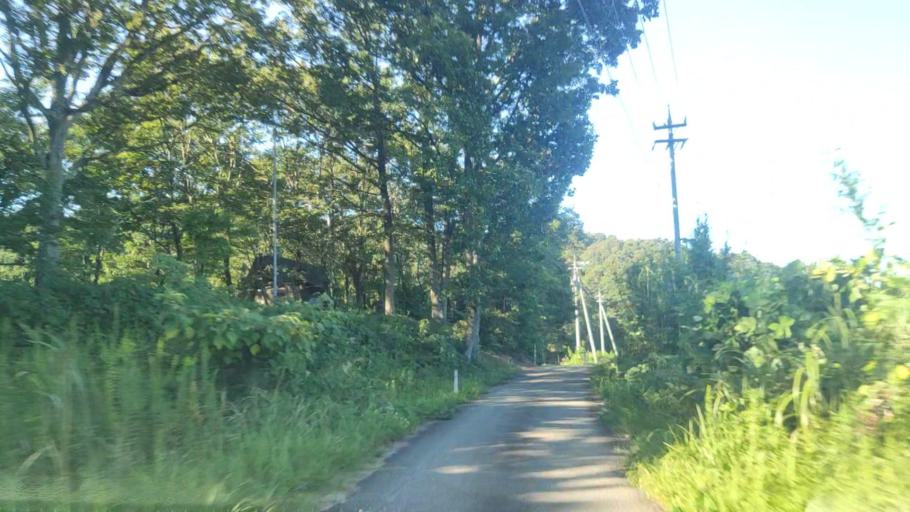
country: JP
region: Ishikawa
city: Nanao
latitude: 37.1231
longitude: 136.8947
